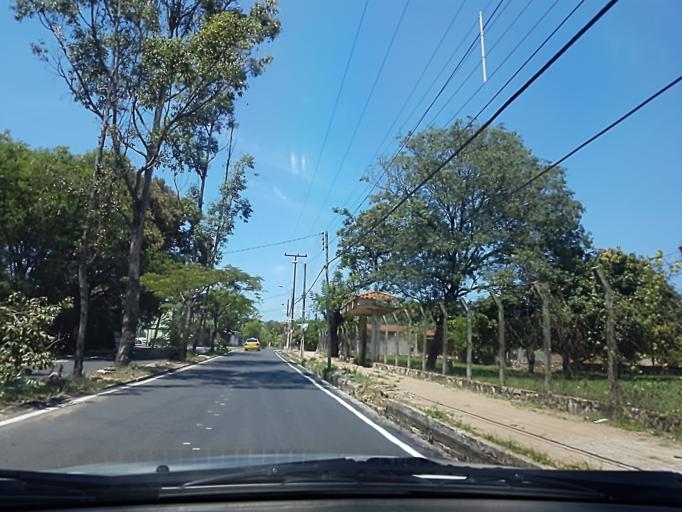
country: PY
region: Central
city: Fernando de la Mora
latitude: -25.2839
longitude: -57.5237
